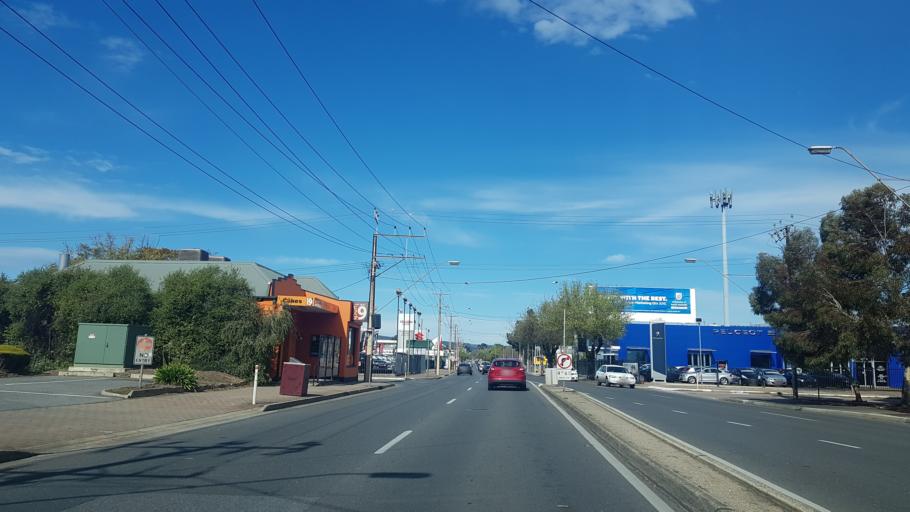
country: AU
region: South Australia
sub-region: Unley
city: Wayville
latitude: -34.9426
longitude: 138.5890
